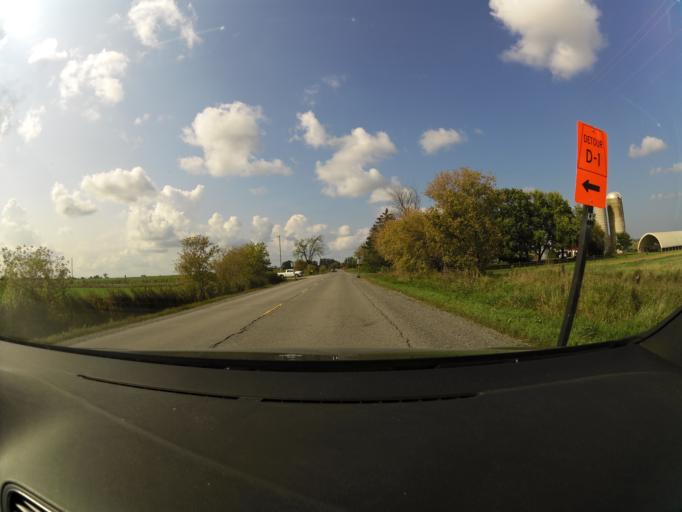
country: CA
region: Ontario
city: Arnprior
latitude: 45.3810
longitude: -76.1747
